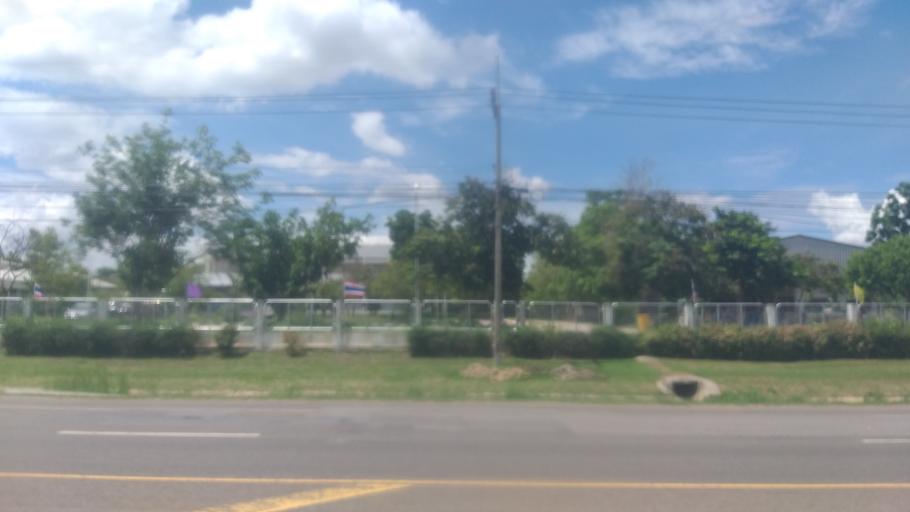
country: TH
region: Nakhon Ratchasima
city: Phra Thong Kham
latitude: 15.2971
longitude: 101.9843
